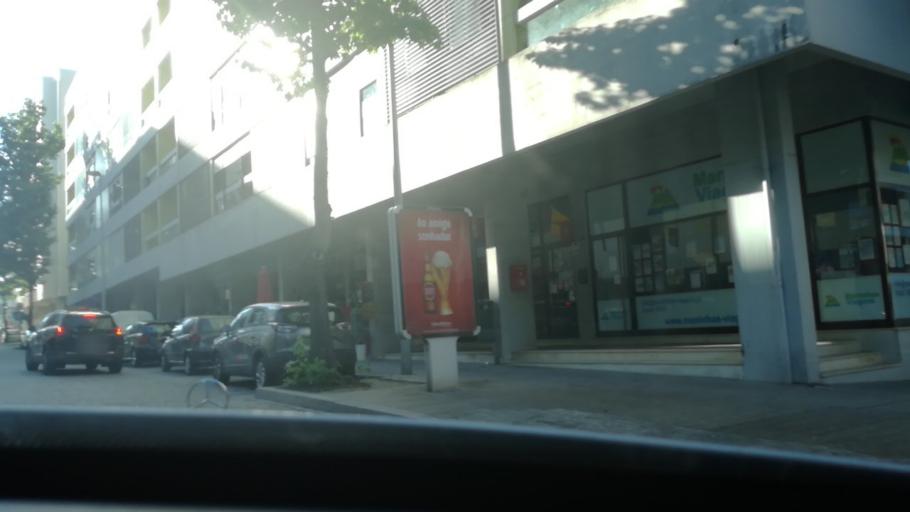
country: PT
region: Porto
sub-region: Maia
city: Maia
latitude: 41.2298
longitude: -8.6120
